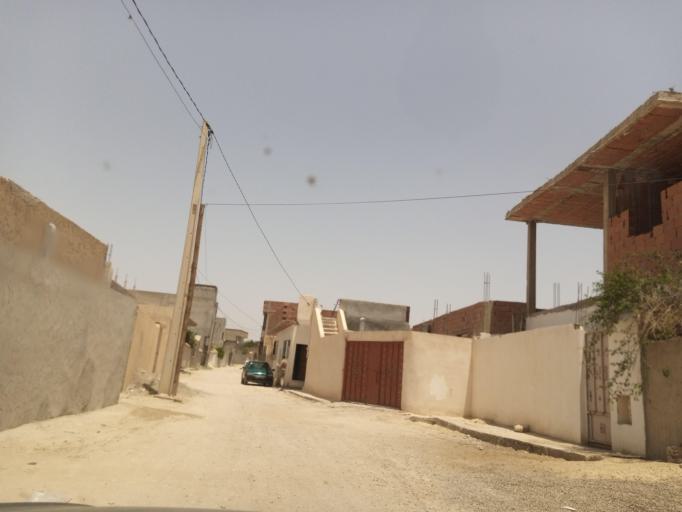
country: TN
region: Al Qasrayn
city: Kasserine
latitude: 35.2129
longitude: 8.8921
